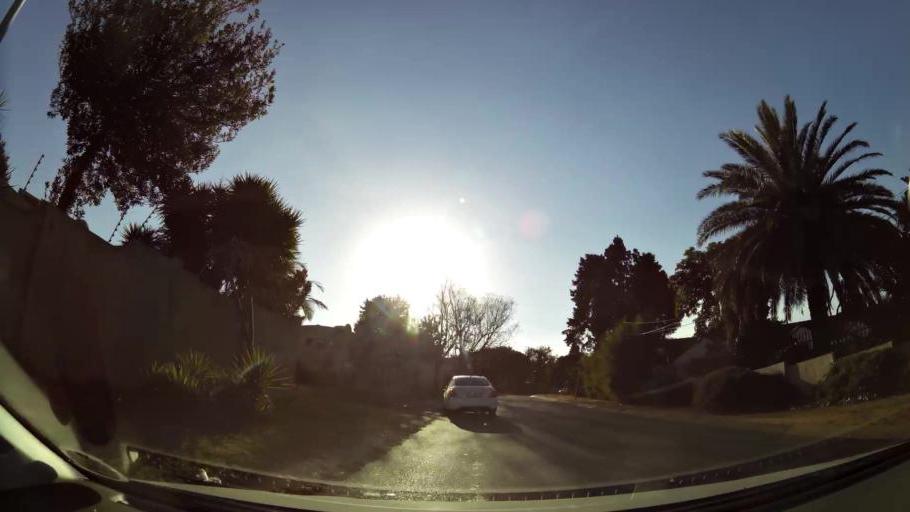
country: ZA
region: Gauteng
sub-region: City of Johannesburg Metropolitan Municipality
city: Modderfontein
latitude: -26.0972
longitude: 28.0687
